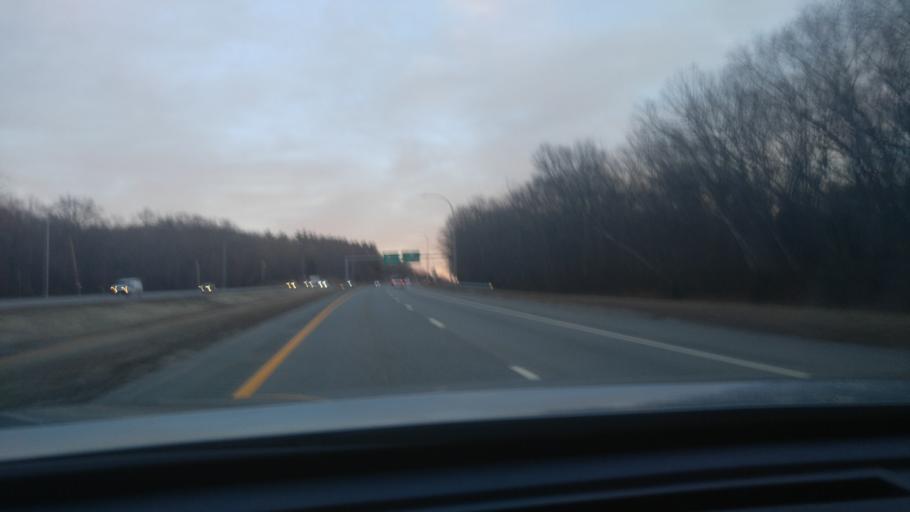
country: US
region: Rhode Island
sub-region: Washington County
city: North Kingstown
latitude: 41.5310
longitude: -71.4582
